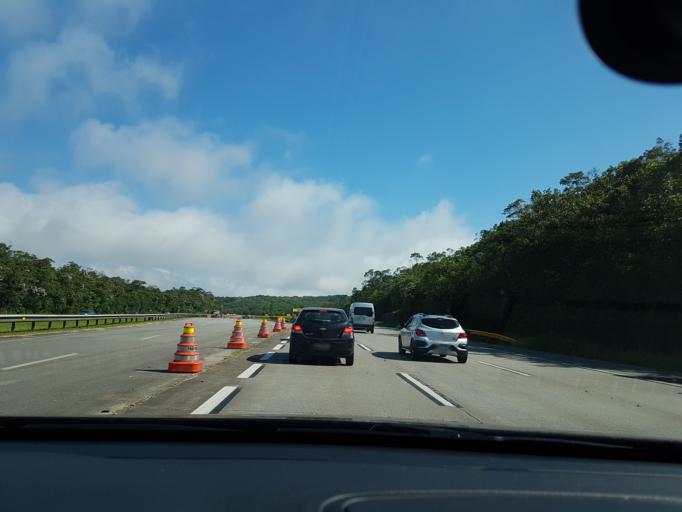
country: BR
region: Sao Paulo
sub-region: Cubatao
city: Cubatao
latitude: -23.9200
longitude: -46.5557
